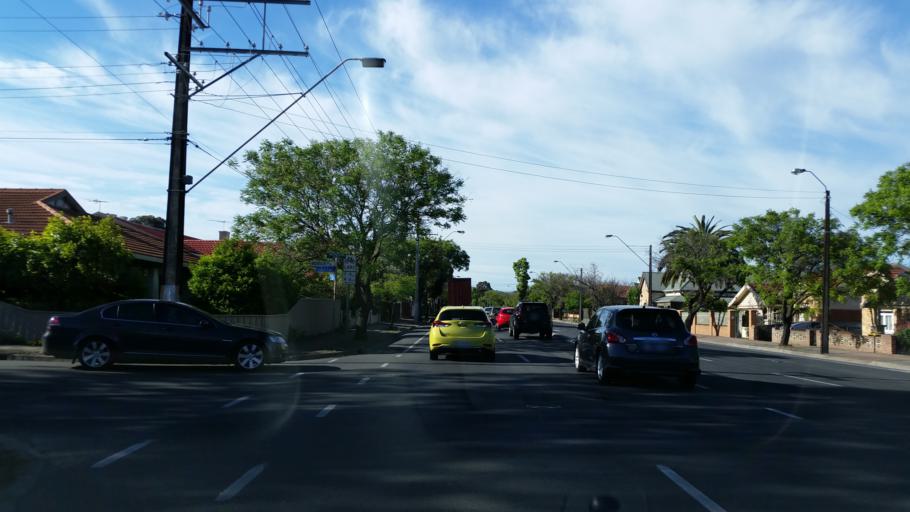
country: AU
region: South Australia
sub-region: Norwood Payneham St Peters
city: Payneham
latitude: -34.8986
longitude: 138.6394
